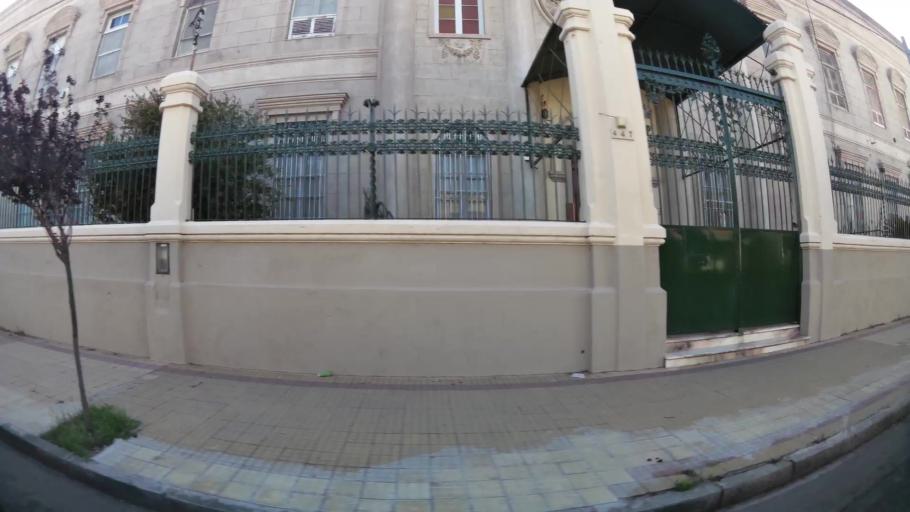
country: AR
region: Cordoba
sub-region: Departamento de Capital
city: Cordoba
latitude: -31.3950
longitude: -64.1742
